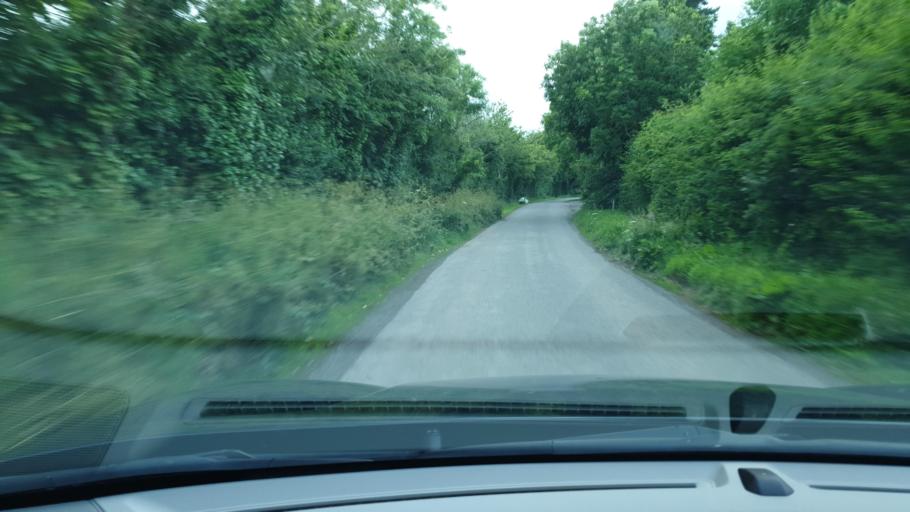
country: IE
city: Kentstown
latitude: 53.5720
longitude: -6.5047
